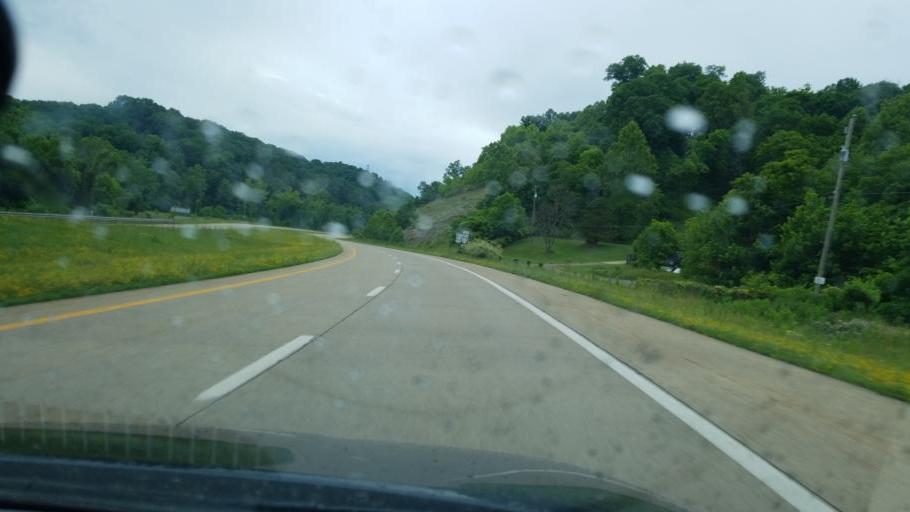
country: US
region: West Virginia
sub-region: Wood County
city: Washington
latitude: 39.2132
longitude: -81.8304
